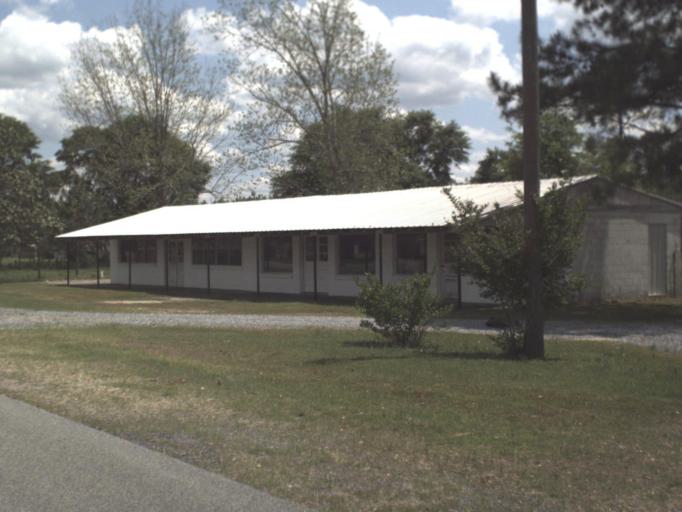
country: US
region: Alabama
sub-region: Escambia County
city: Atmore
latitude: 30.8876
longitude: -87.4588
